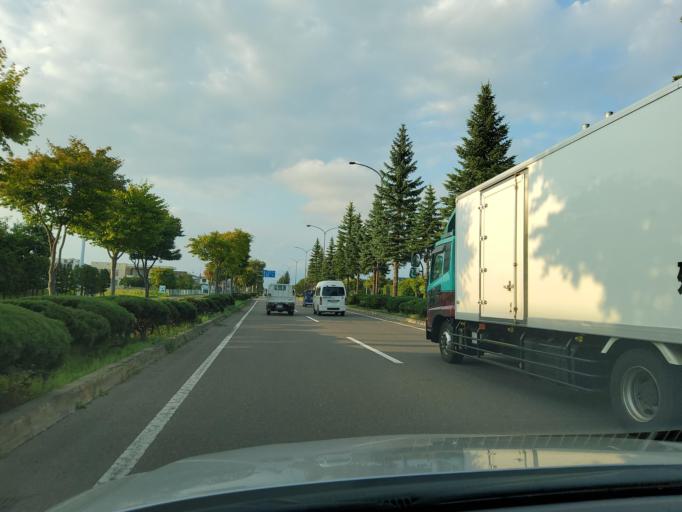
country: JP
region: Hokkaido
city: Obihiro
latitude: 42.9300
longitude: 143.1632
